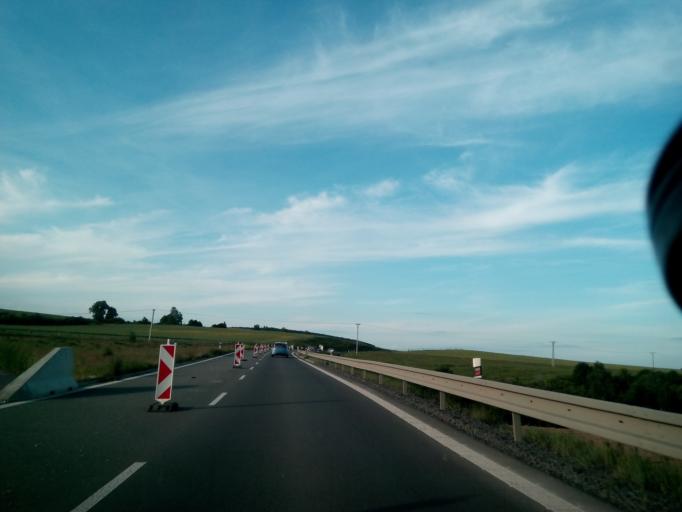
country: SK
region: Presovsky
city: Sabinov
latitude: 49.0007
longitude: 21.1094
